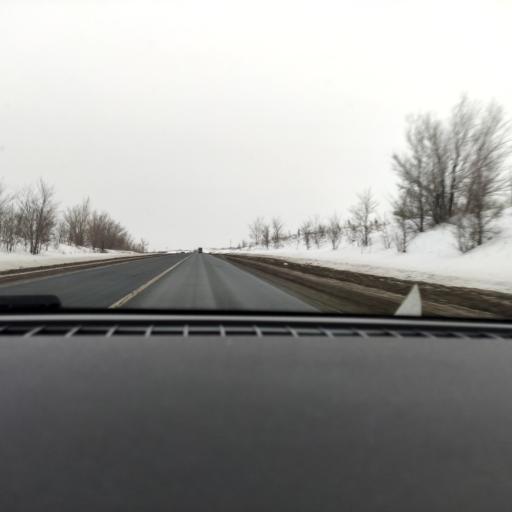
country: RU
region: Samara
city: Smyshlyayevka
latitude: 53.2843
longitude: 50.4614
